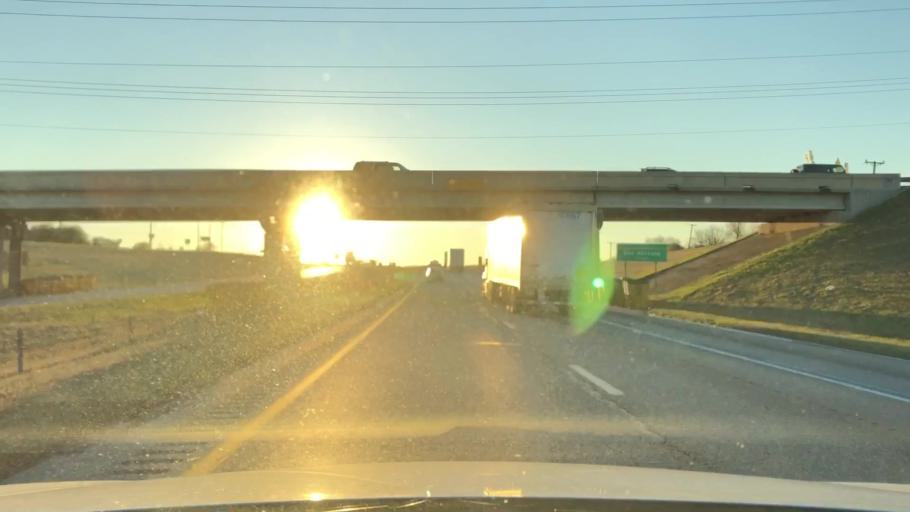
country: US
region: Texas
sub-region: Guadalupe County
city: Cibolo
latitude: 29.4886
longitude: -98.2223
